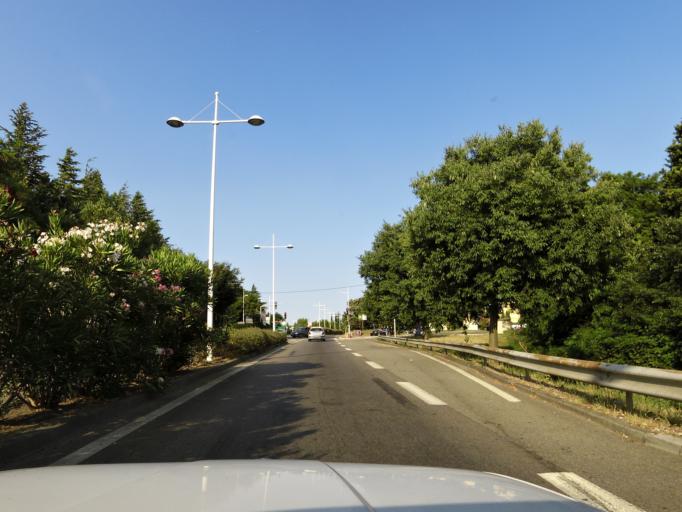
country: FR
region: Provence-Alpes-Cote d'Azur
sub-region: Departement du Vaucluse
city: Bollene
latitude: 44.2879
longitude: 4.7459
